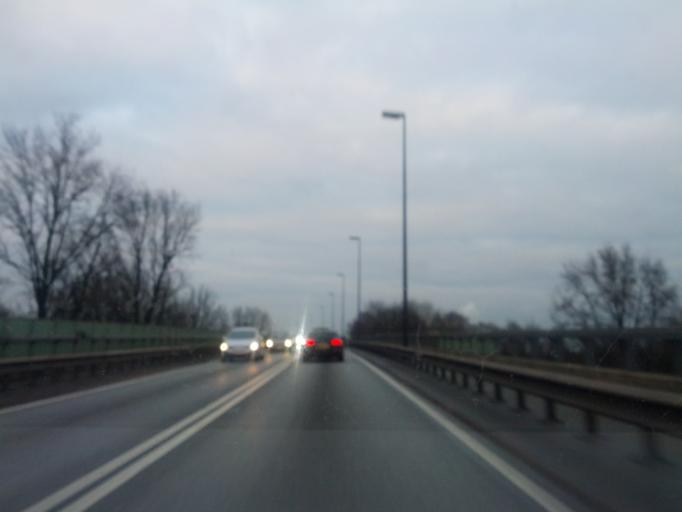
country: DE
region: Bremen
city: Bremen
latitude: 53.1023
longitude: 8.7996
